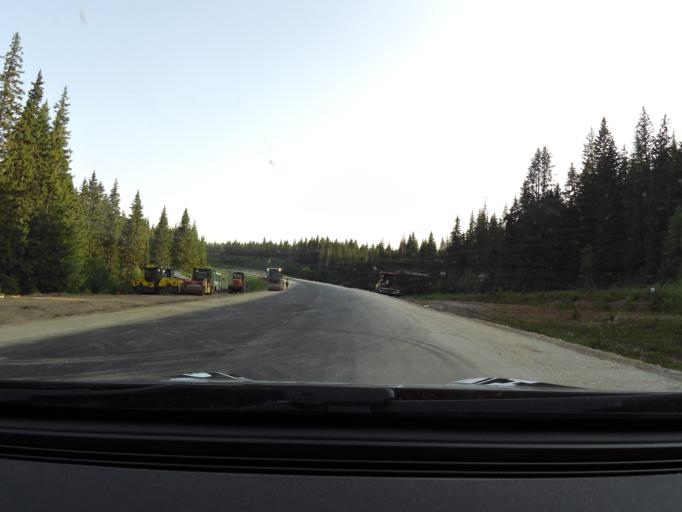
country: RU
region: Sverdlovsk
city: Nizhniye Sergi
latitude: 56.6689
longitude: 59.2698
